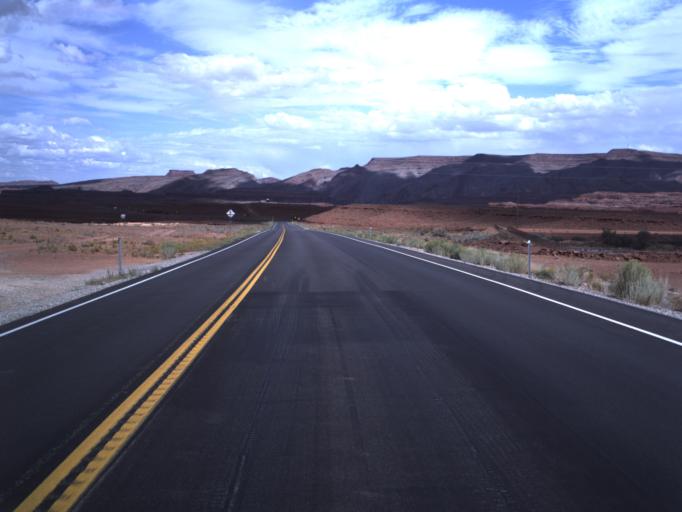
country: US
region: Arizona
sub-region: Navajo County
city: Kayenta
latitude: 37.1338
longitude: -109.8867
